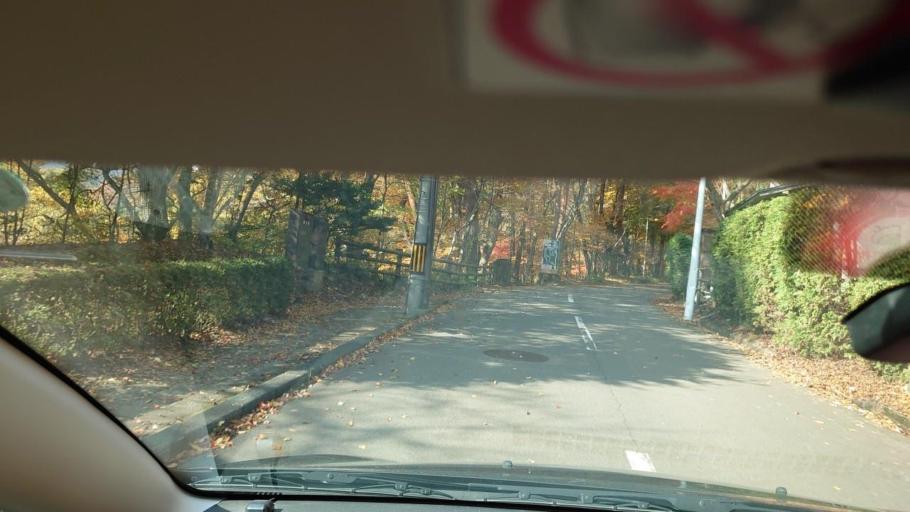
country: JP
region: Iwate
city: Hanamaki
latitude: 39.4536
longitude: 141.0684
